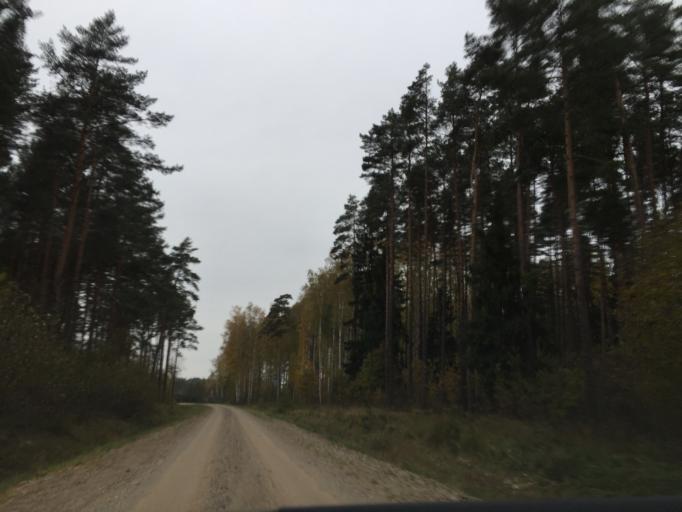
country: LV
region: Jelgava
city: Jelgava
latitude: 56.6366
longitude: 23.6290
